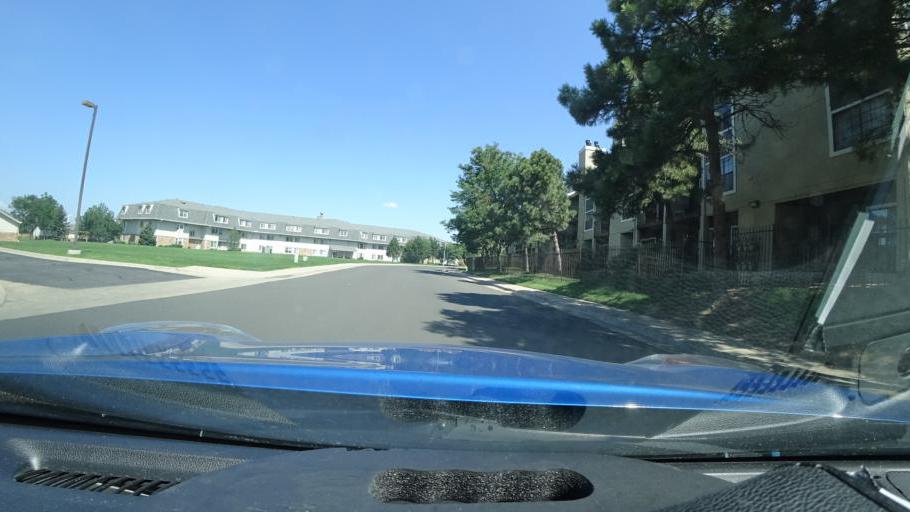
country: US
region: Colorado
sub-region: Adams County
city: Aurora
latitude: 39.7119
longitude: -104.8623
